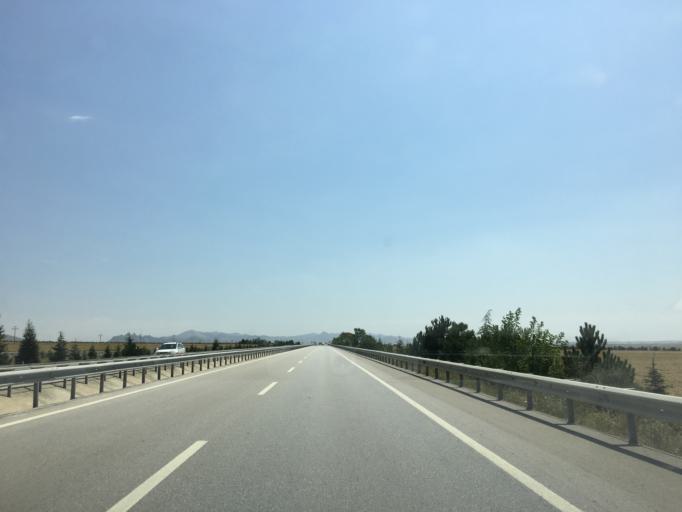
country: TR
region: Eskisehir
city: Sivrihisar
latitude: 39.4599
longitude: 31.3831
